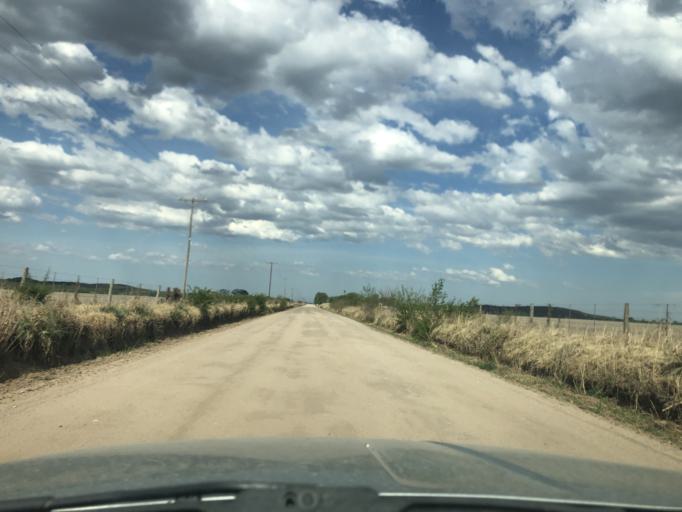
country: AR
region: Cordoba
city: Jesus Maria
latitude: -31.0120
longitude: -64.1485
